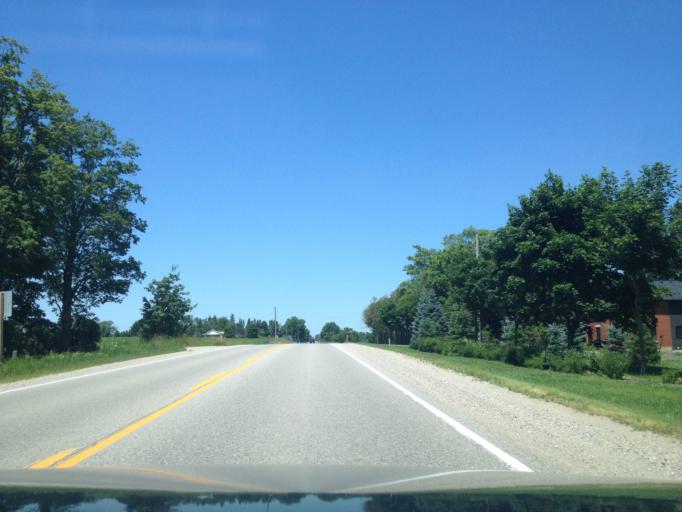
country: CA
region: Ontario
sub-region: Wellington County
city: Guelph
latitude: 43.6218
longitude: -80.2229
